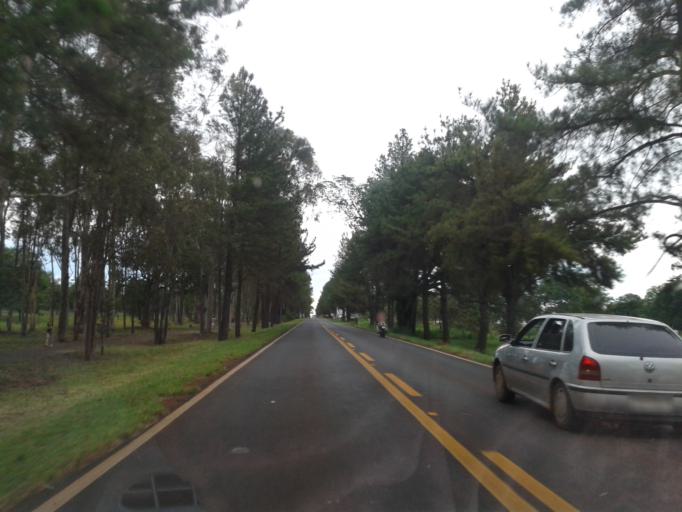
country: BR
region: Minas Gerais
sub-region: Santa Vitoria
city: Santa Vitoria
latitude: -18.8702
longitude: -50.1242
